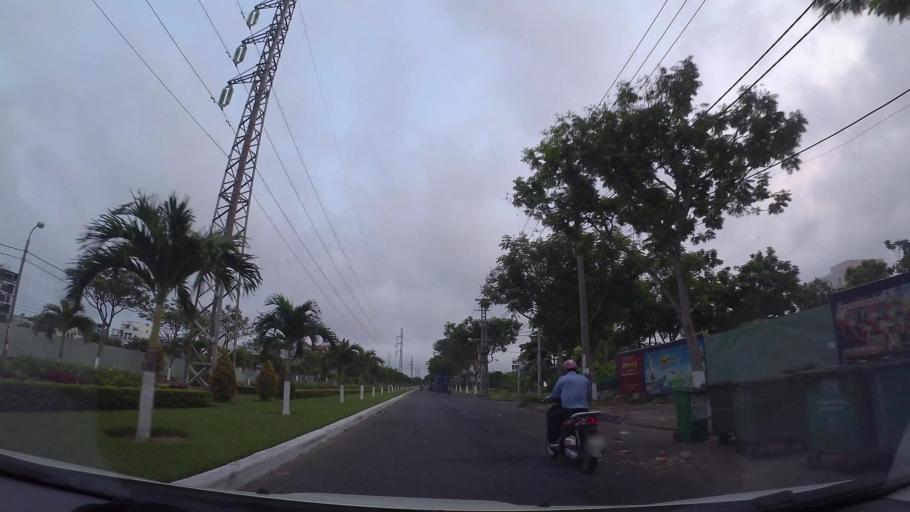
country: VN
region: Da Nang
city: Son Tra
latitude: 16.0427
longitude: 108.2378
